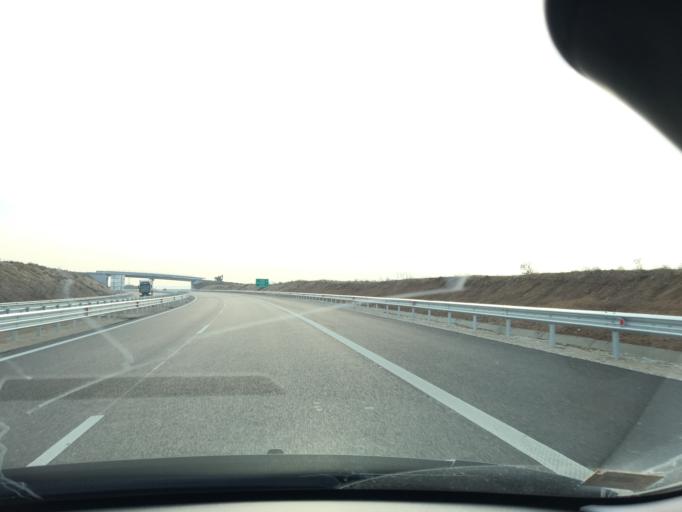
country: BG
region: Blagoevgrad
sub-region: Obshtina Sandanski
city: Sandanski
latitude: 41.5340
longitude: 23.2583
